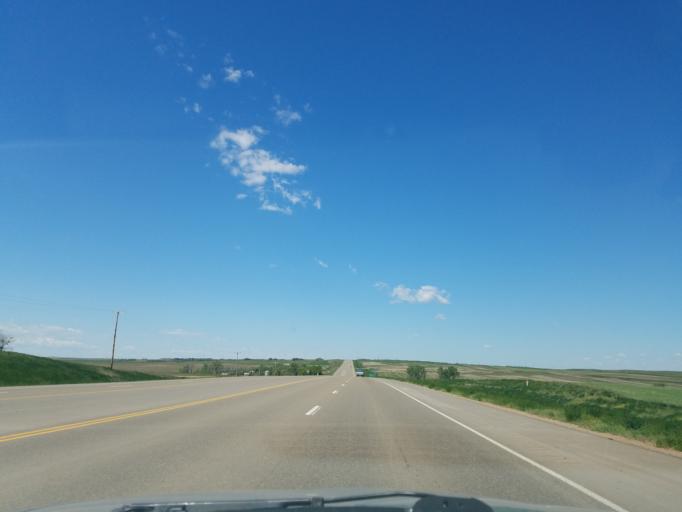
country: US
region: North Dakota
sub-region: McKenzie County
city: Watford City
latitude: 47.8049
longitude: -103.4484
